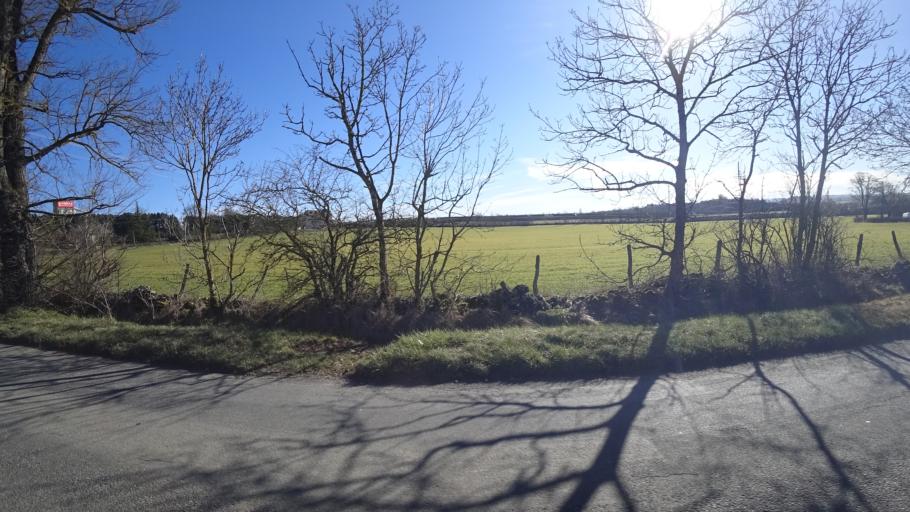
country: FR
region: Midi-Pyrenees
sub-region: Departement de l'Aveyron
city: Sebazac-Concoures
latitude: 44.3869
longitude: 2.5903
